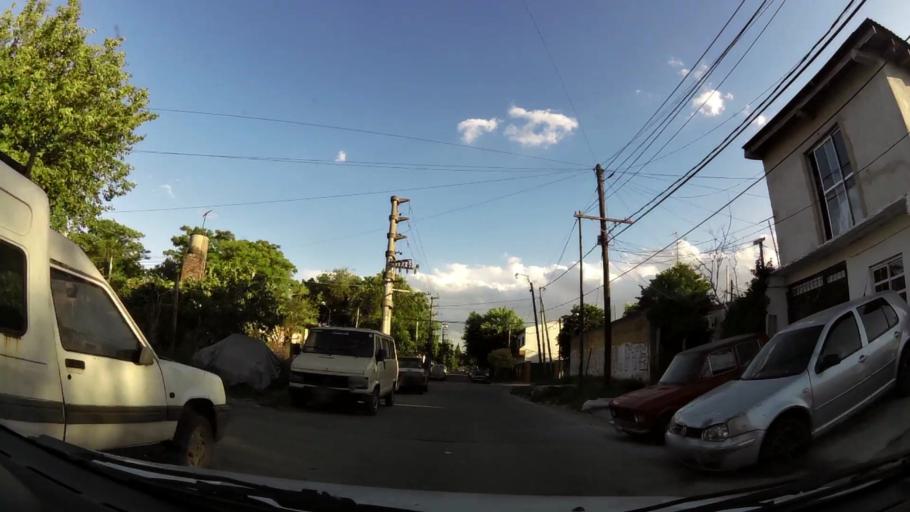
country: AR
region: Buenos Aires
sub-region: Partido de San Isidro
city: San Isidro
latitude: -34.4673
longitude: -58.5512
